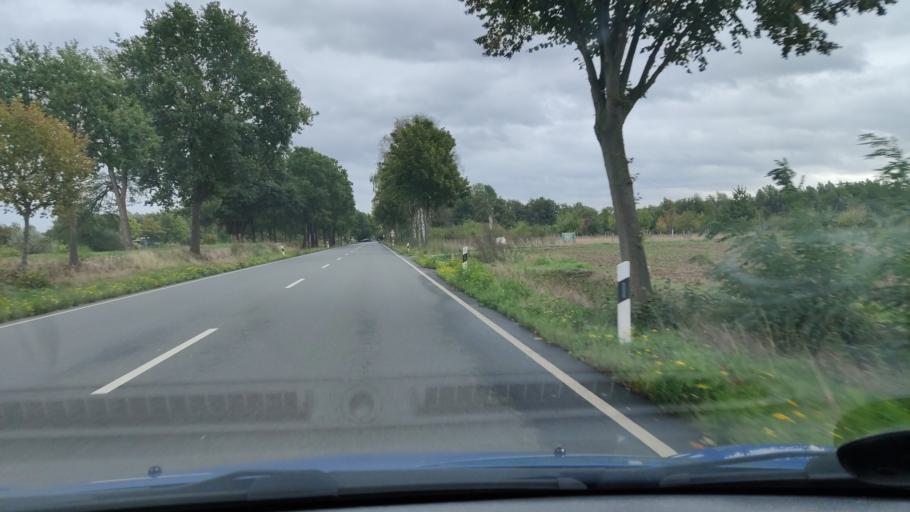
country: DE
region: Lower Saxony
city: Seelze
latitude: 52.3932
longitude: 9.5711
